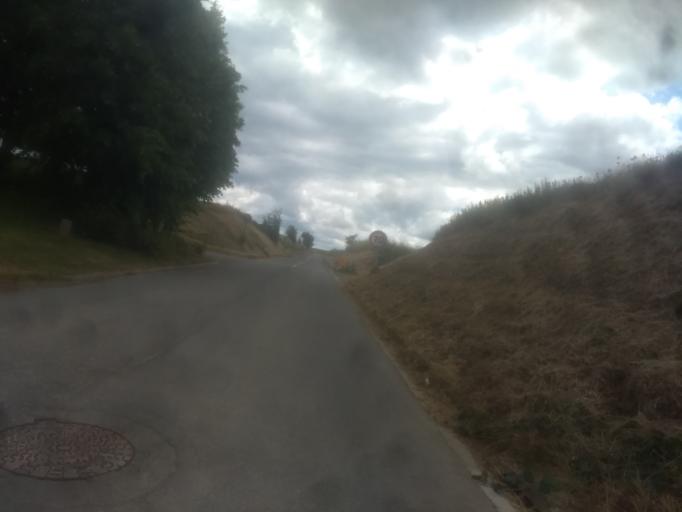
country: FR
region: Nord-Pas-de-Calais
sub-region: Departement du Pas-de-Calais
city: Riviere
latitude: 50.2434
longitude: 2.7270
